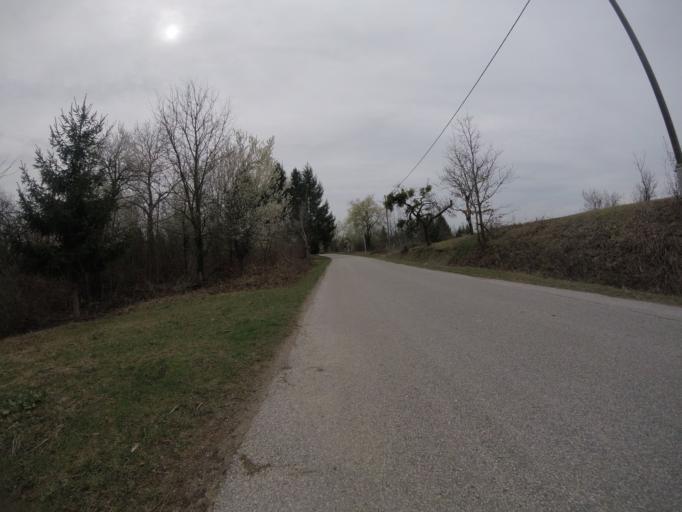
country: HR
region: Zagrebacka
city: Lukavec
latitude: 45.5478
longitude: 15.9826
